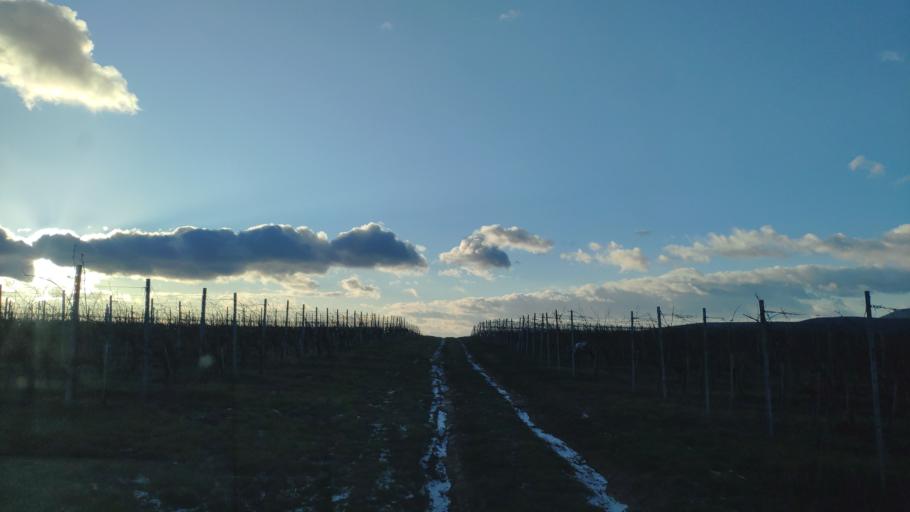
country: HU
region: Borsod-Abauj-Zemplen
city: Tolcsva
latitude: 48.2830
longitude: 21.4804
